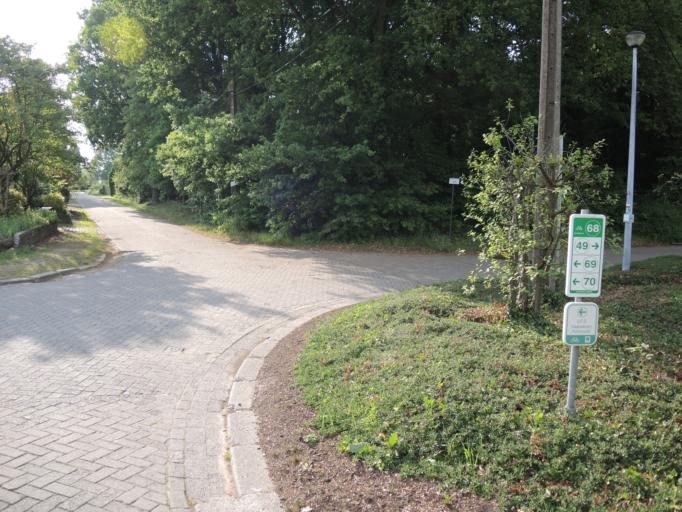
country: BE
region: Flanders
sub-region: Provincie Antwerpen
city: Vosselaar
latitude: 51.3195
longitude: 4.8877
